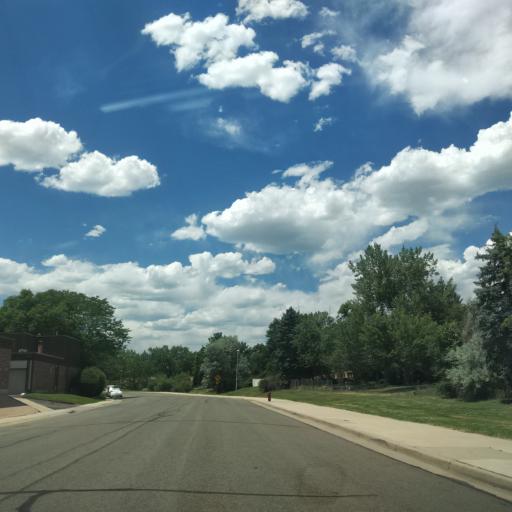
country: US
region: Colorado
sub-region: Jefferson County
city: Lakewood
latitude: 39.6835
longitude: -105.1016
